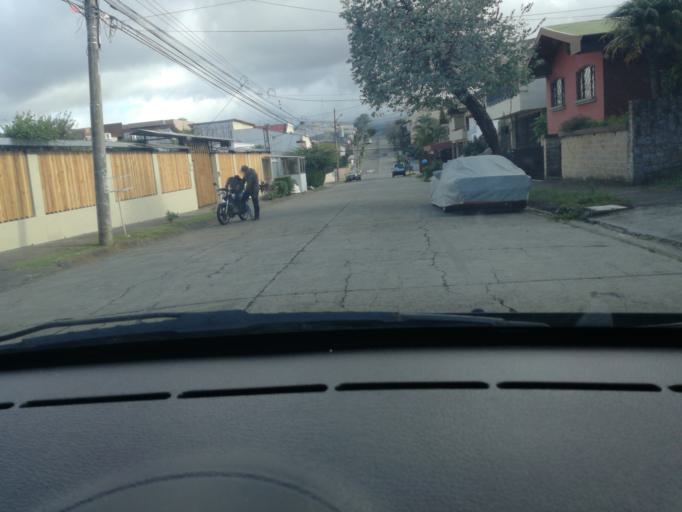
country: CR
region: San Jose
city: San Pedro
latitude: 9.9278
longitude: -84.0450
